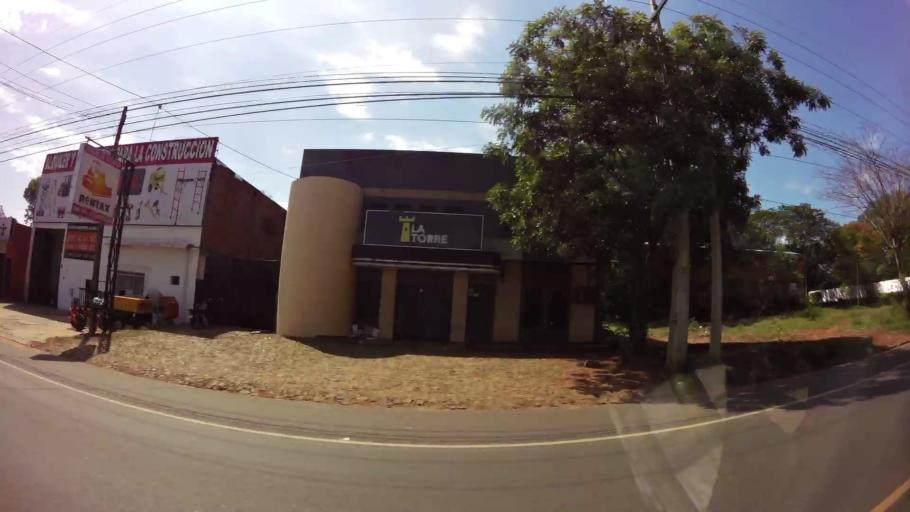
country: PY
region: Central
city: San Lorenzo
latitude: -25.2835
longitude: -57.4990
